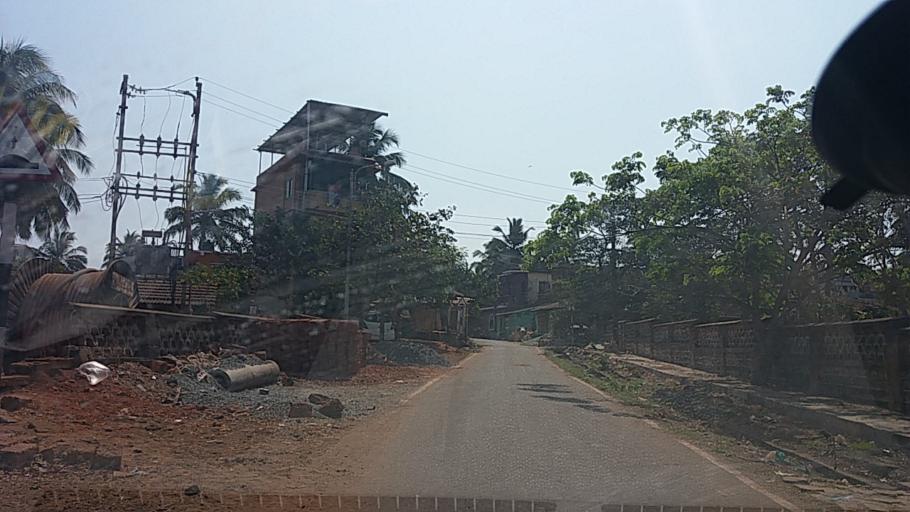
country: IN
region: Goa
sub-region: South Goa
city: Marmagao
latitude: 15.4077
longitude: 73.7910
